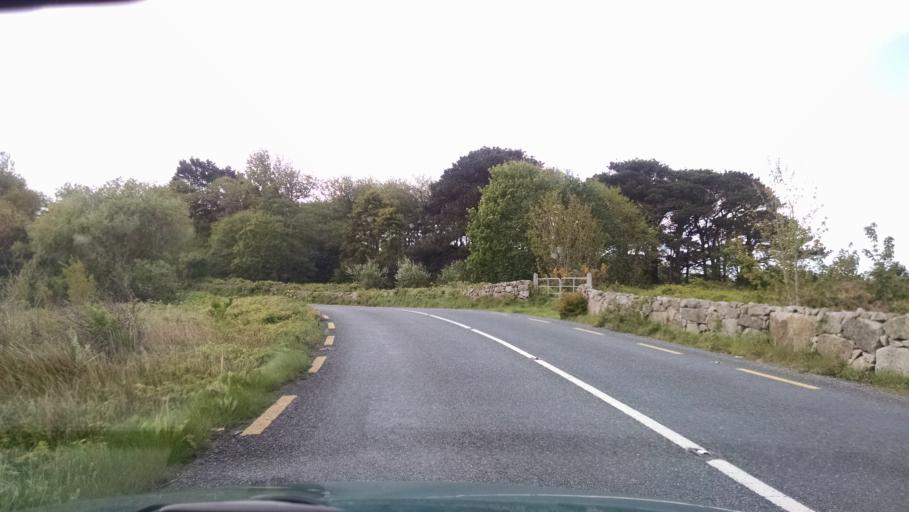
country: IE
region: Connaught
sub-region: County Galway
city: Oughterard
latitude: 53.3120
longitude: -9.6258
